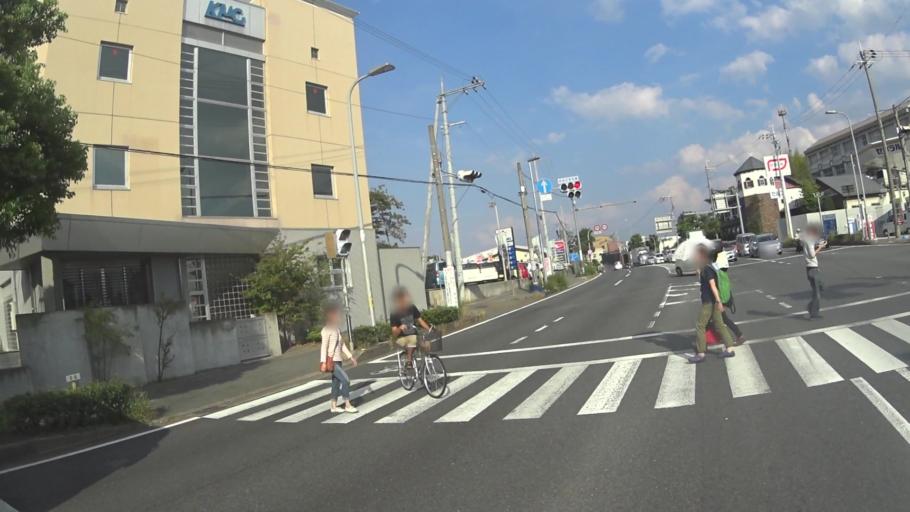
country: JP
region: Kyoto
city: Muko
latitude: 34.9706
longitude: 135.6789
